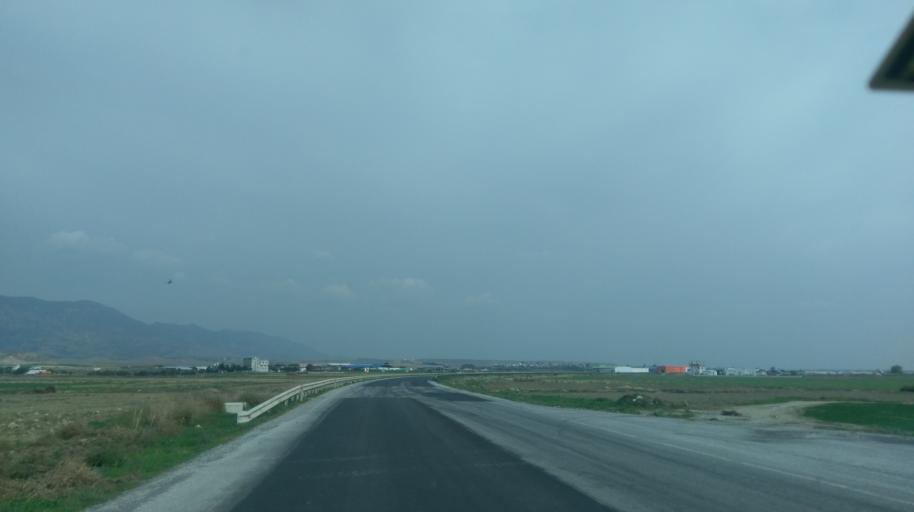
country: CY
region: Lefkosia
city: Geri
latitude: 35.2250
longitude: 33.5208
